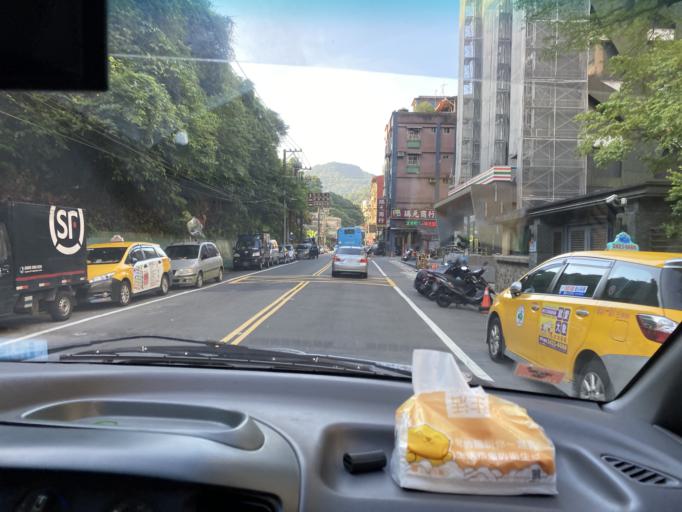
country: TW
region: Taiwan
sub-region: Keelung
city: Keelung
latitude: 25.0958
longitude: 121.7389
